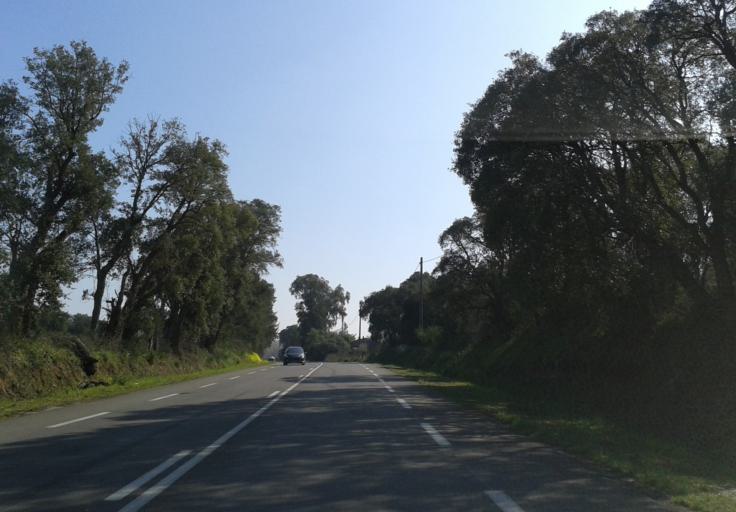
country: FR
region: Corsica
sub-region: Departement de la Haute-Corse
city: Cervione
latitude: 42.2973
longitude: 9.5456
